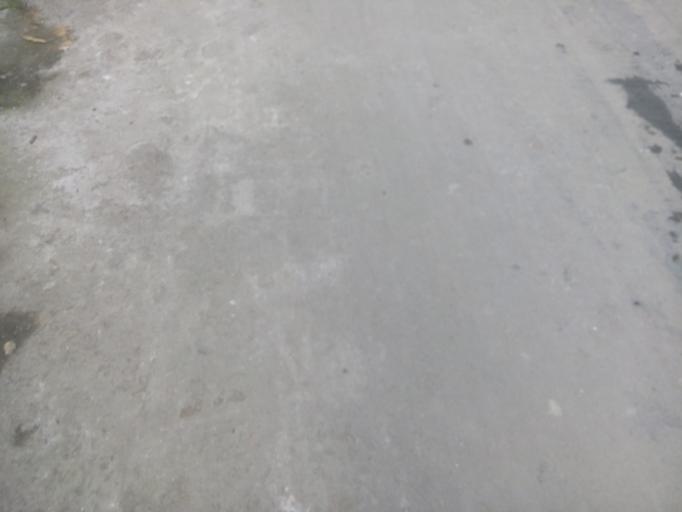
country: IN
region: West Bengal
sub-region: South 24 Paraganas
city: Santoshpur
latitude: 22.4605
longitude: 88.3095
